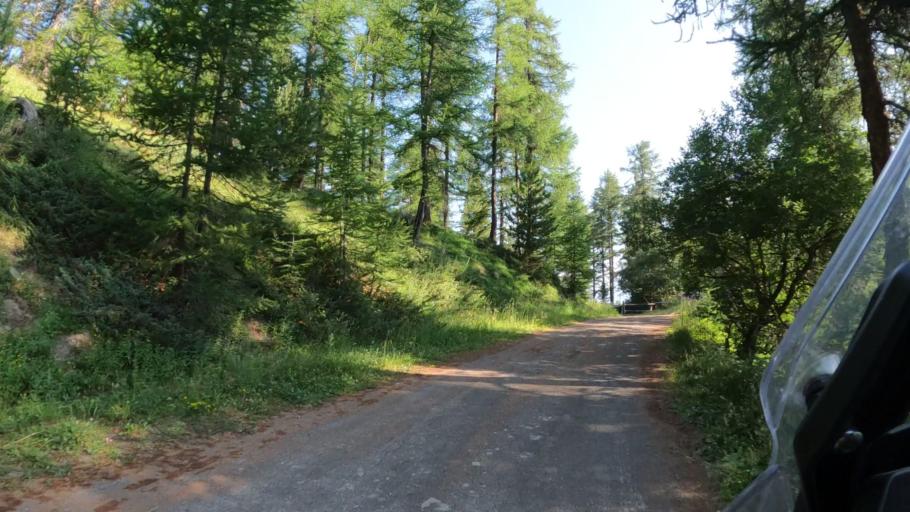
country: FR
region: Provence-Alpes-Cote d'Azur
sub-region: Departement des Hautes-Alpes
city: Guillestre
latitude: 44.6195
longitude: 6.6431
